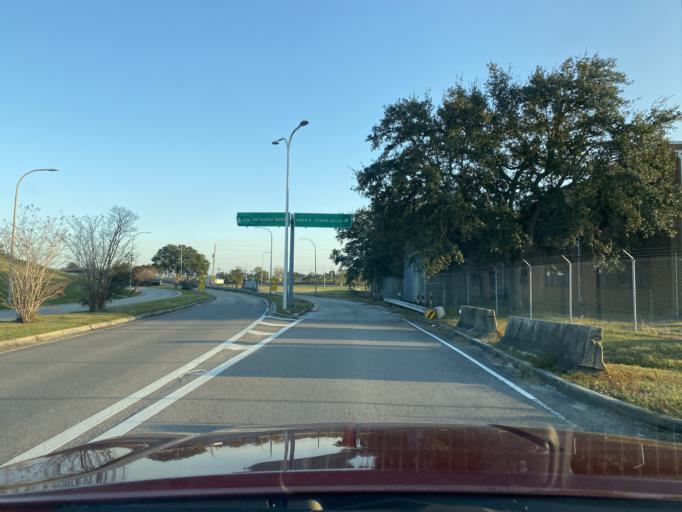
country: US
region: Louisiana
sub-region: Orleans Parish
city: New Orleans
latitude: 30.0318
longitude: -90.0408
